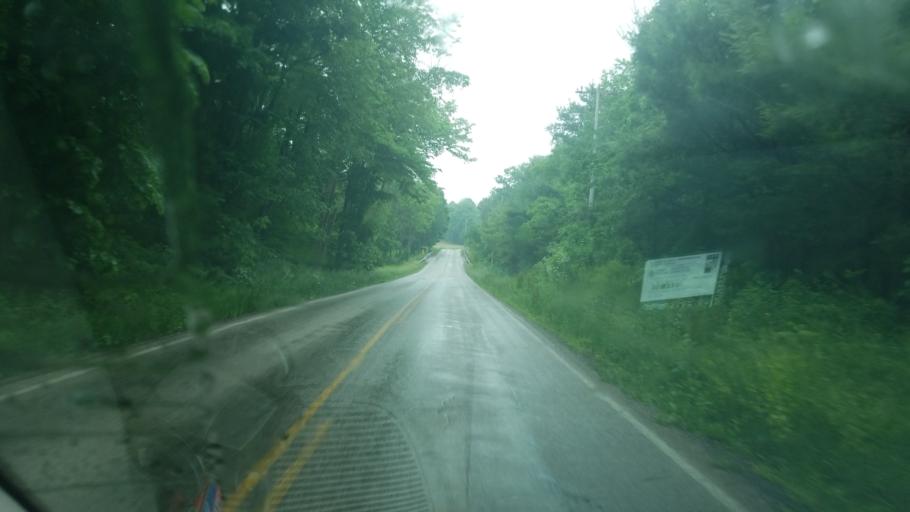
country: US
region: Ohio
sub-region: Sandusky County
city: Bellville
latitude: 40.6821
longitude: -82.4628
